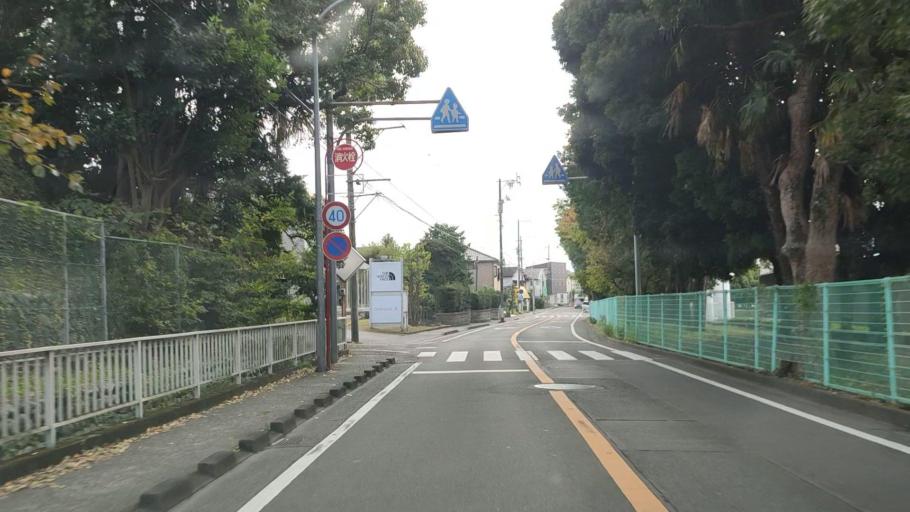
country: JP
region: Shizuoka
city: Shizuoka-shi
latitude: 34.9885
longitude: 138.4314
